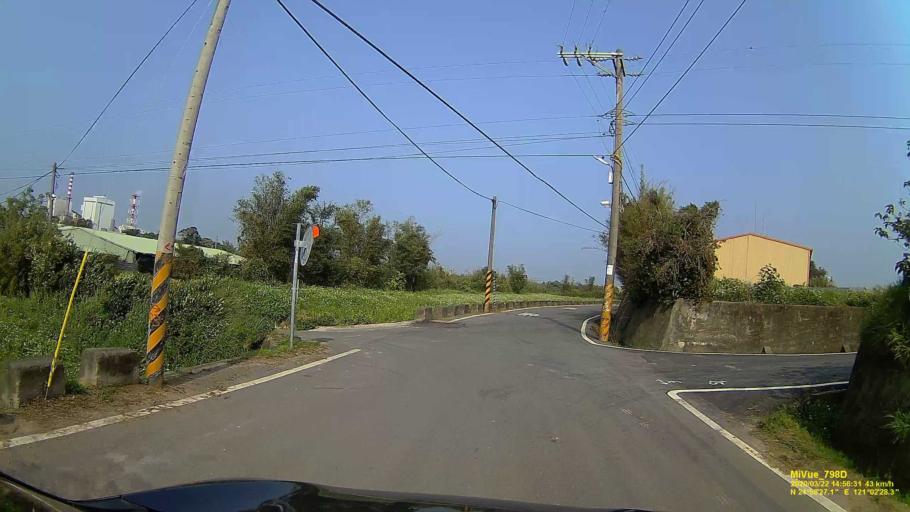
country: TW
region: Taiwan
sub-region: Hsinchu
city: Zhubei
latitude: 24.9740
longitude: 121.0415
